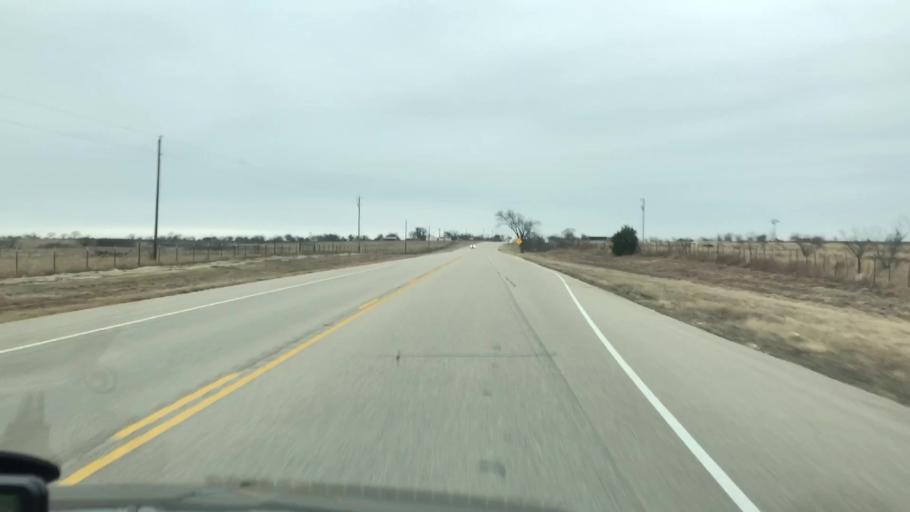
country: US
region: Texas
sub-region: Hamilton County
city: Hico
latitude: 31.8673
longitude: -98.1093
